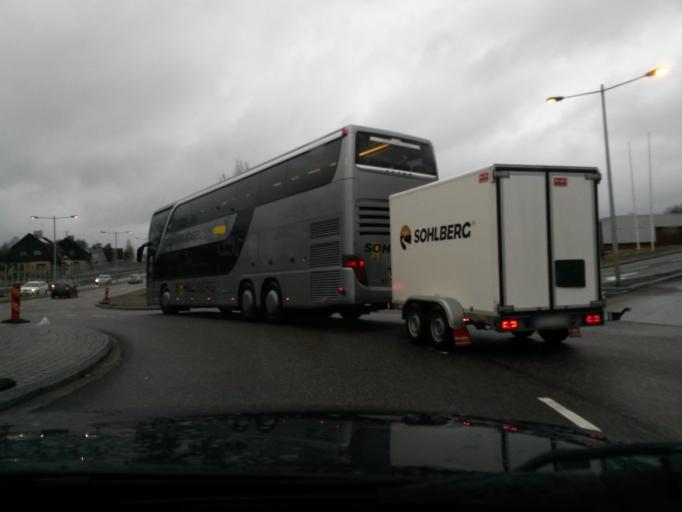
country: SE
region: Vaestra Goetaland
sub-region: Boras Kommun
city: Boras
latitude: 57.7383
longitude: 12.9375
